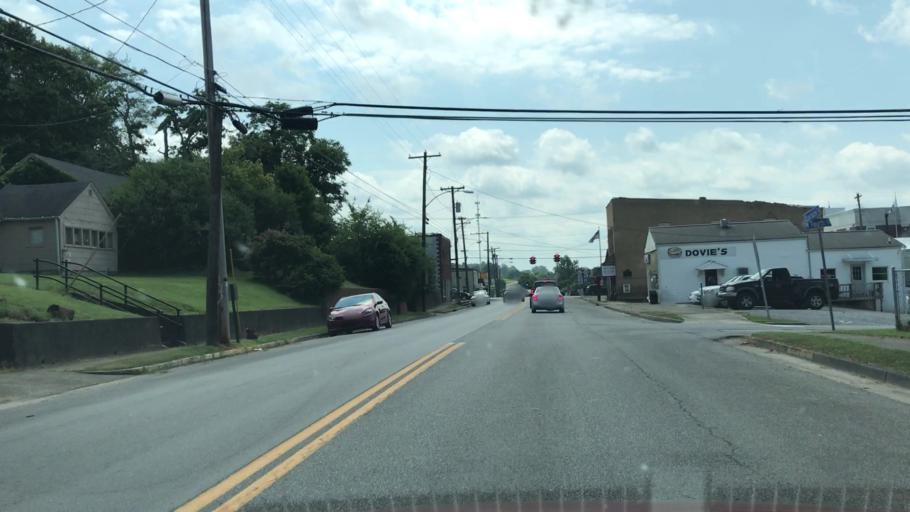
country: US
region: Kentucky
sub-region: Monroe County
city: Tompkinsville
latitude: 36.7030
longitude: -85.6927
